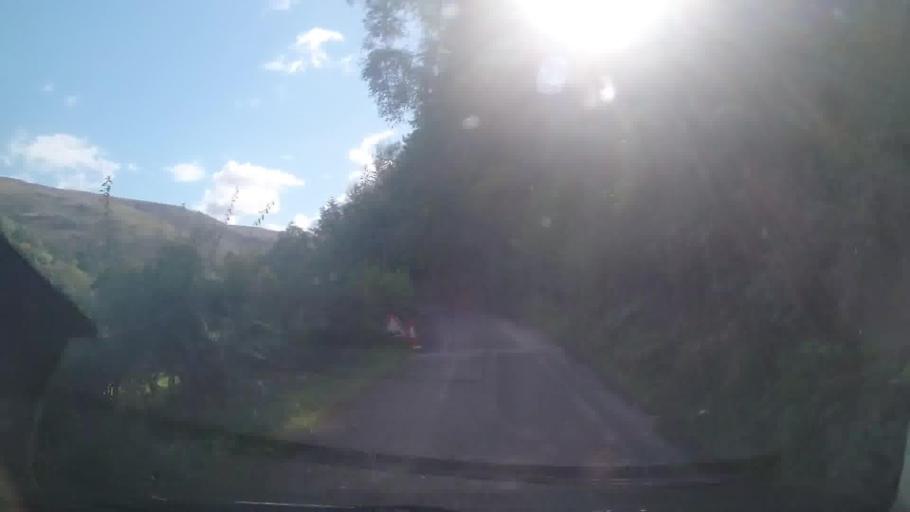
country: GB
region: Wales
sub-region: Gwynedd
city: Bala
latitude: 52.7646
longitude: -3.6241
